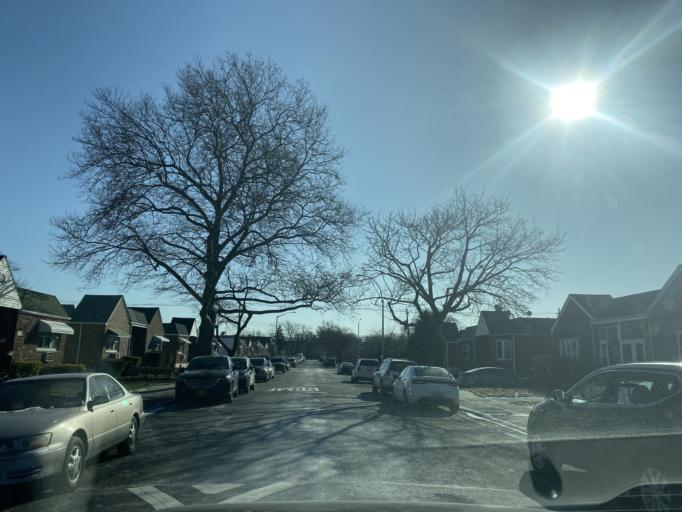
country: US
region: New York
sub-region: Bronx
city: The Bronx
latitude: 40.8293
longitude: -73.8319
